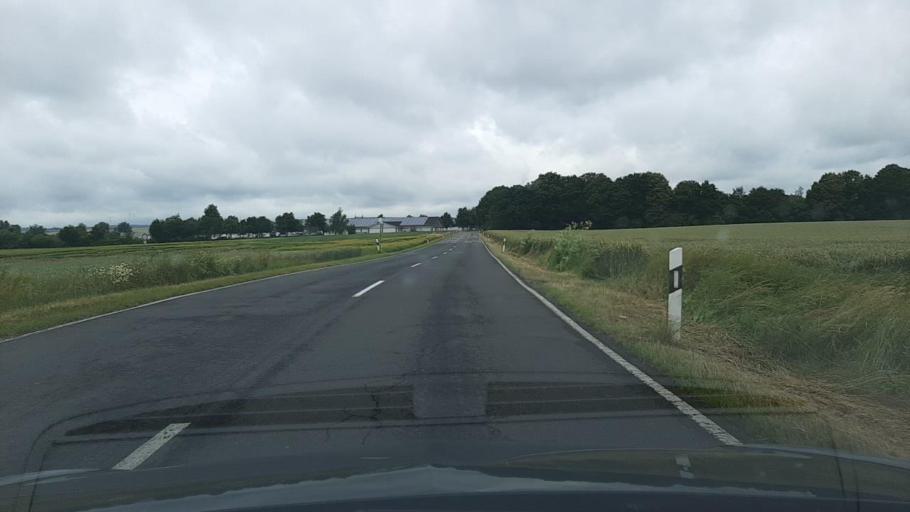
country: DE
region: Rheinland-Pfalz
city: Polch
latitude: 50.3057
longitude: 7.3335
